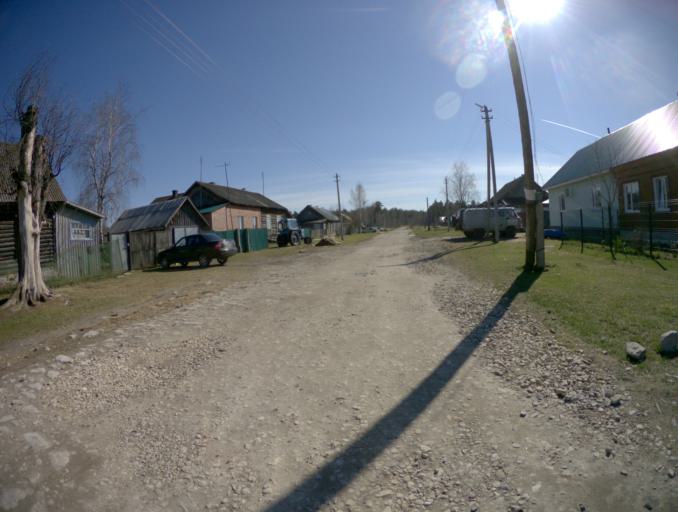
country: RU
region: Vladimir
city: Ivanishchi
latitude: 55.7712
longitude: 40.4199
